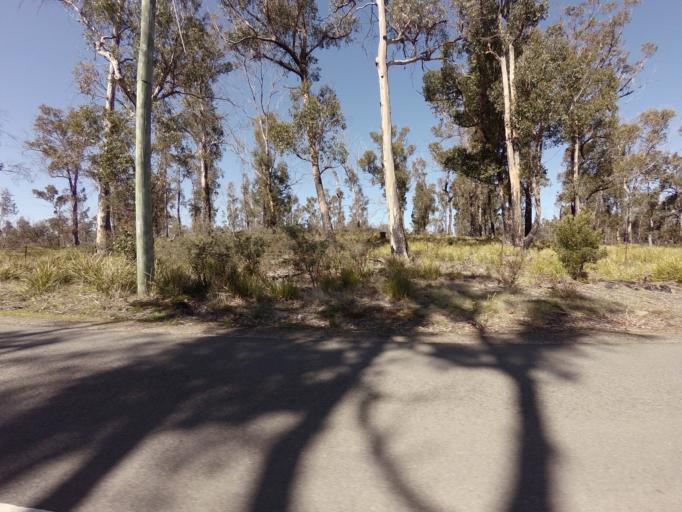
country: AU
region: Tasmania
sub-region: Derwent Valley
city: New Norfolk
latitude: -42.5544
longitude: 146.7119
